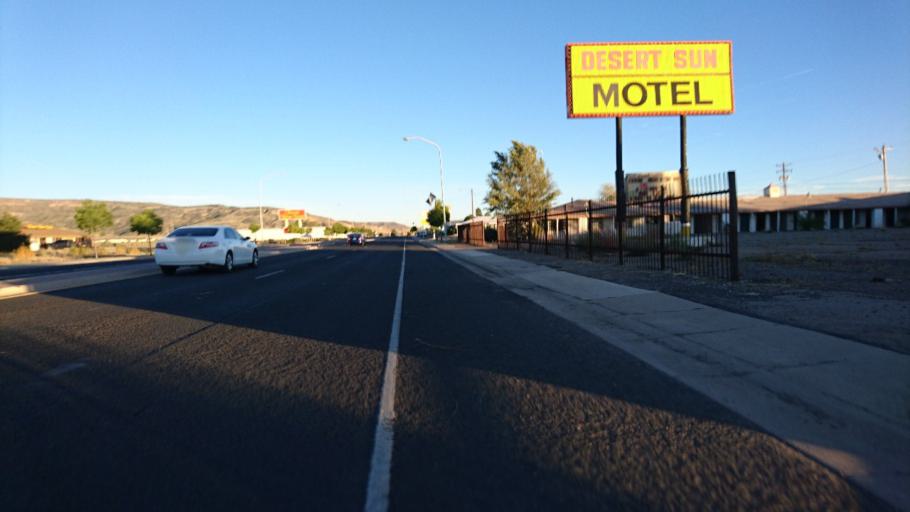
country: US
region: New Mexico
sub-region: Cibola County
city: Grants
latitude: 35.1431
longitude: -107.8355
